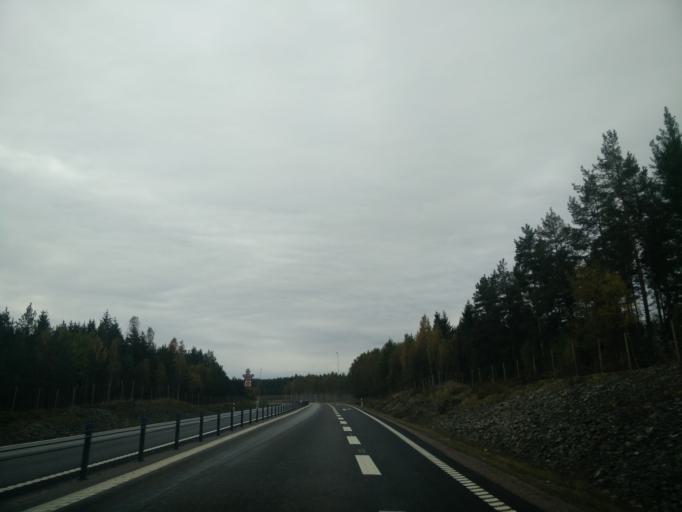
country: SE
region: Gaevleborg
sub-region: Gavle Kommun
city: Norrsundet
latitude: 60.9070
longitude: 17.0147
